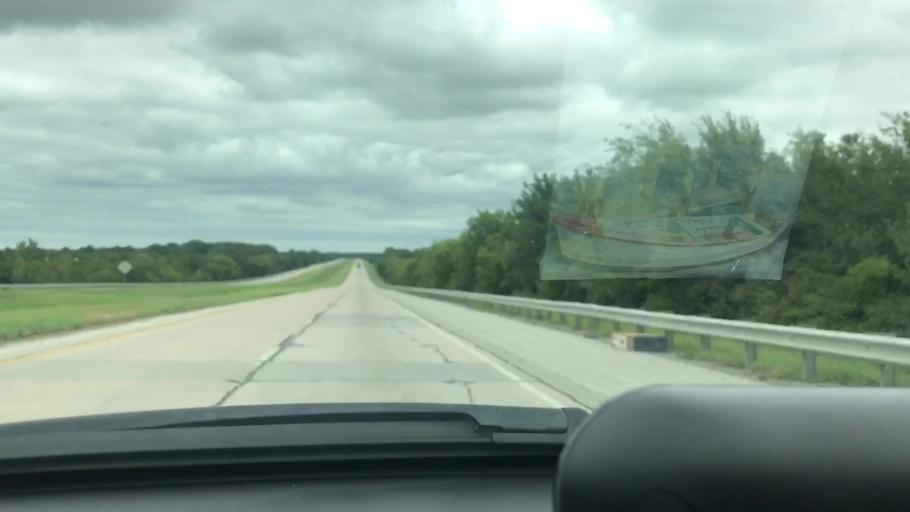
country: US
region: Oklahoma
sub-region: Wagoner County
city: Wagoner
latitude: 35.8885
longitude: -95.4025
